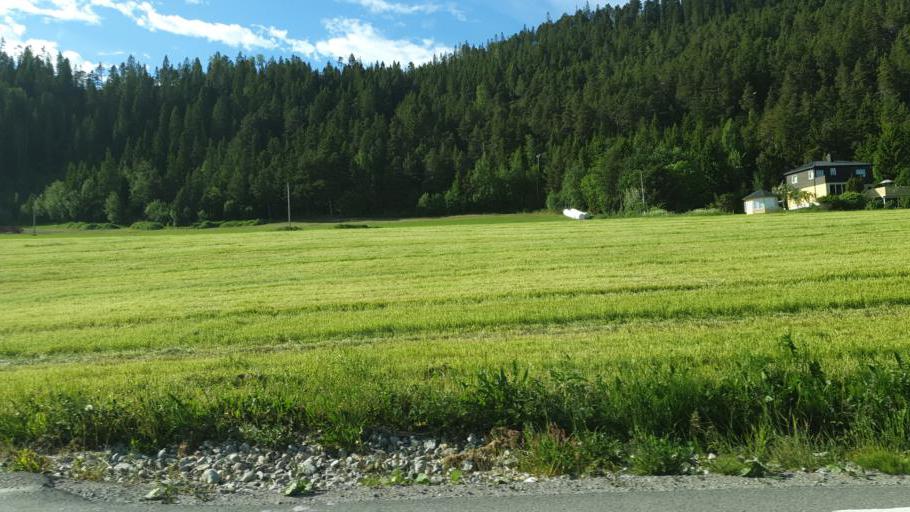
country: NO
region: Sor-Trondelag
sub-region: Rissa
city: Rissa
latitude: 63.5001
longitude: 10.1195
